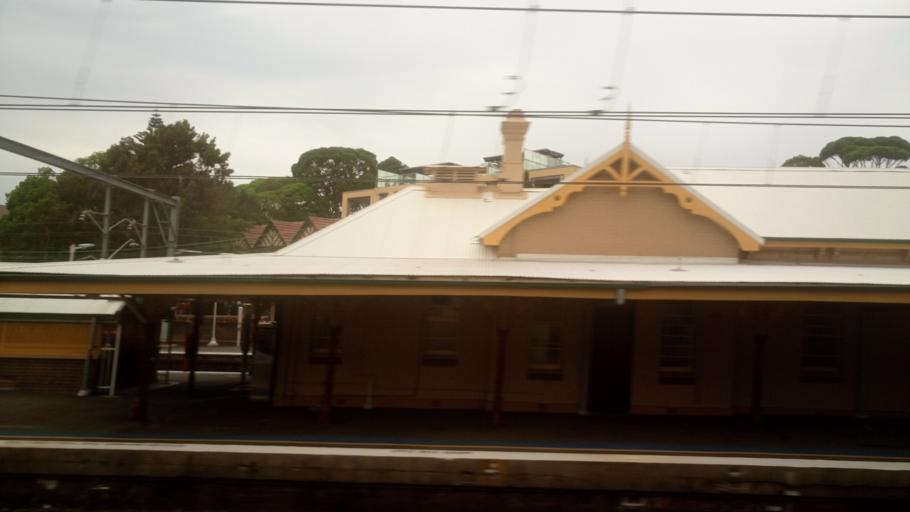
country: AU
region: New South Wales
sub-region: Marrickville
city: Camperdown
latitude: -33.8943
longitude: 151.1638
